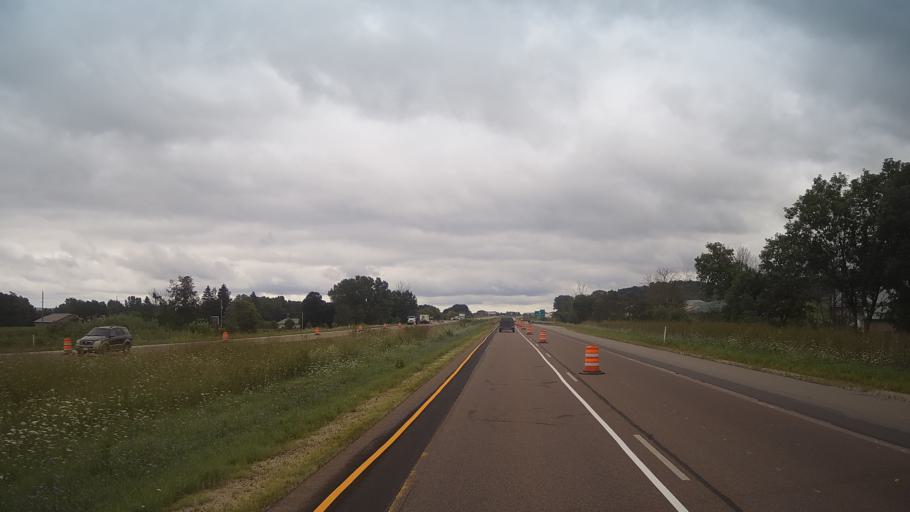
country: US
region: Wisconsin
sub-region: La Crosse County
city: West Salem
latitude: 43.8875
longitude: -91.1041
